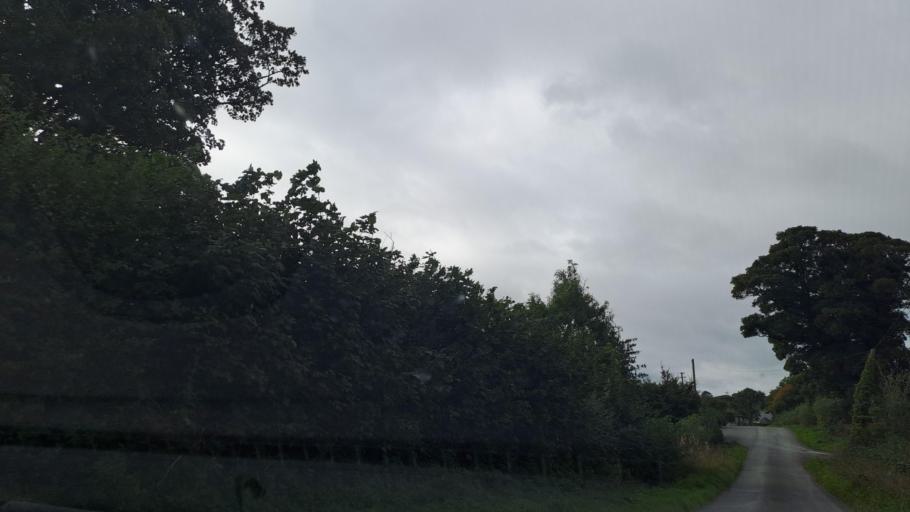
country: IE
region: Ulster
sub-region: An Cabhan
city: Bailieborough
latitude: 53.9705
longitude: -6.8953
